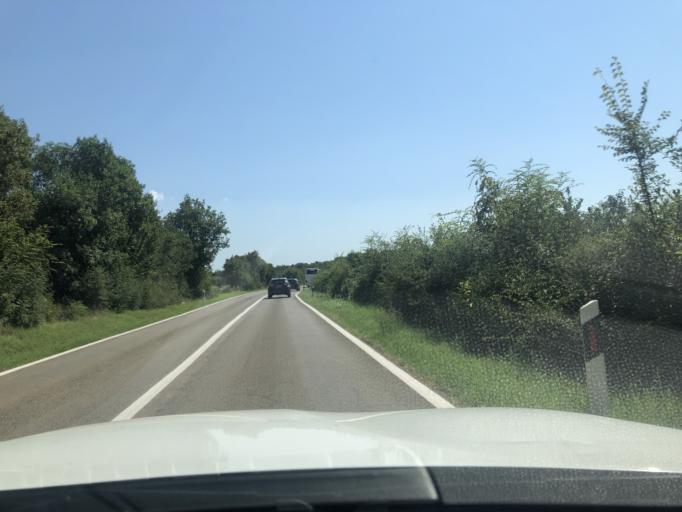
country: HR
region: Istarska
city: Vodnjan
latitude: 45.0296
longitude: 13.7963
